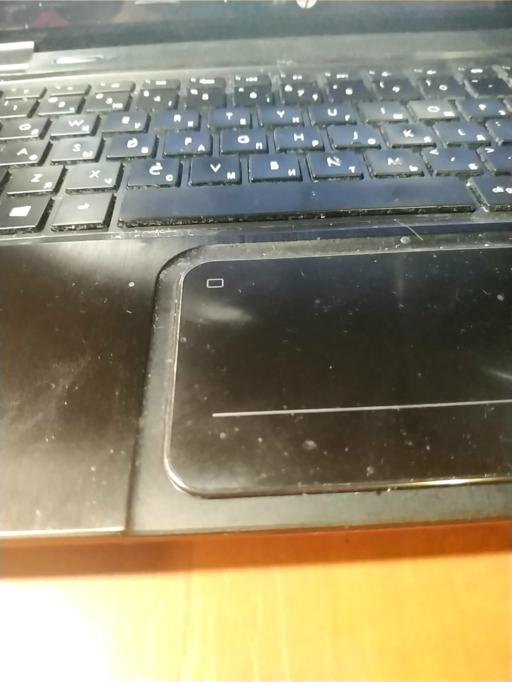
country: RU
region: Tverskaya
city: Rameshki
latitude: 57.2320
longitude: 35.9390
